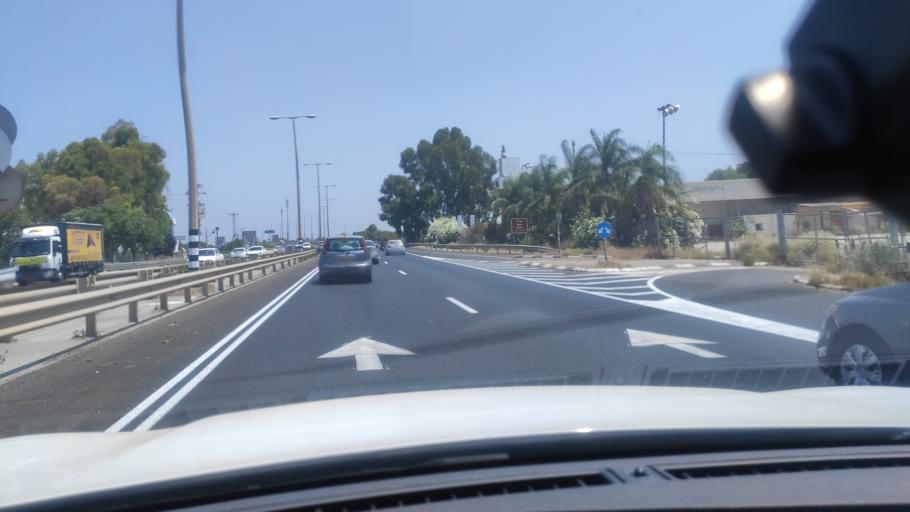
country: IL
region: Central District
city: Petah Tiqwa
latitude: 32.1068
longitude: 34.9004
